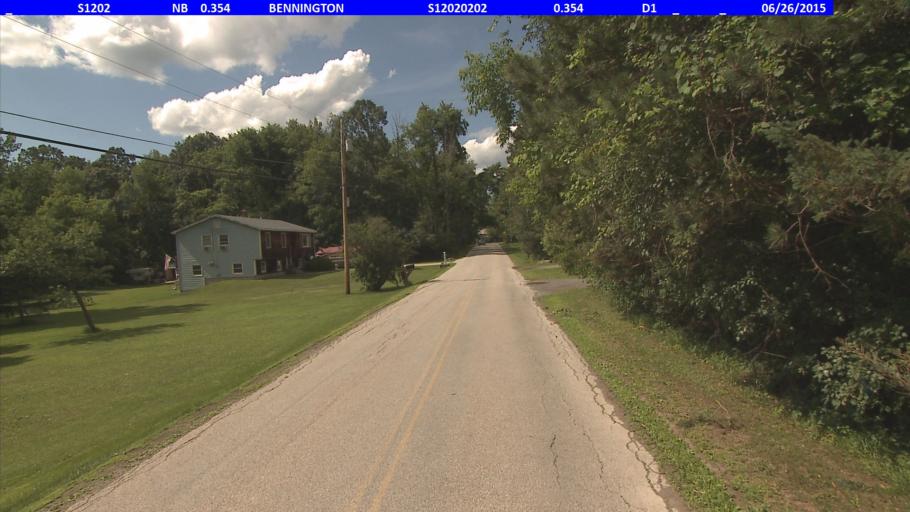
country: US
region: Vermont
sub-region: Bennington County
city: North Bennington
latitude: 42.9242
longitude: -73.2268
